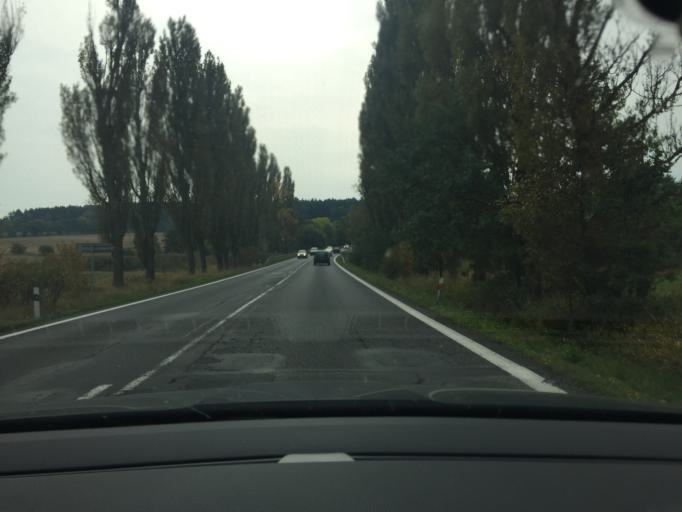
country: CZ
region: Central Bohemia
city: Milin
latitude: 49.5909
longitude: 14.0704
